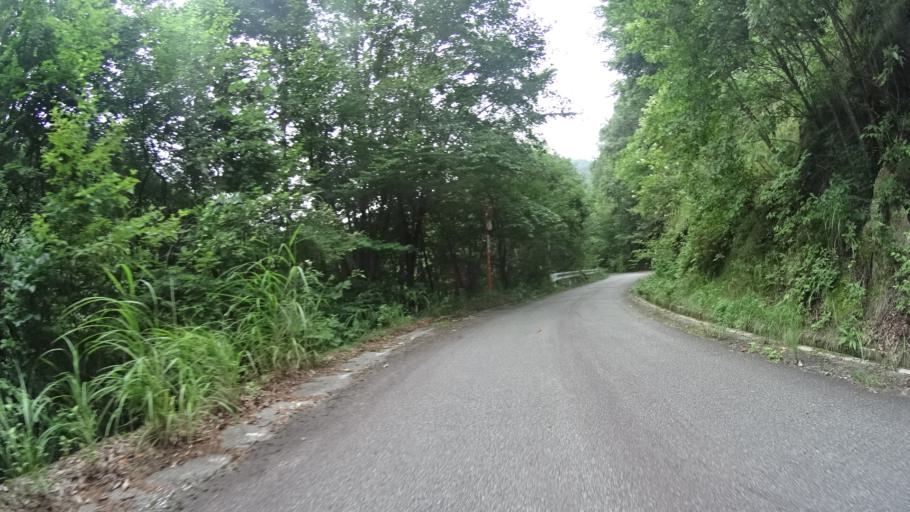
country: JP
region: Yamanashi
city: Kofu-shi
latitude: 35.8090
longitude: 138.6155
